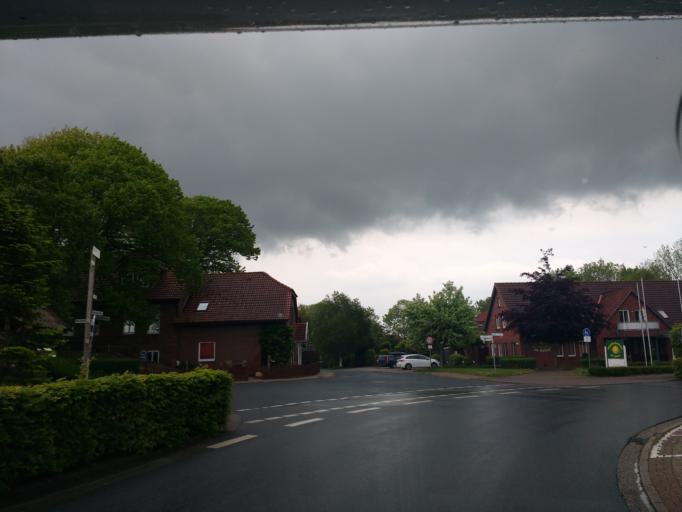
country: DE
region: Lower Saxony
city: Wangerooge
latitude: 53.6987
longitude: 7.8996
